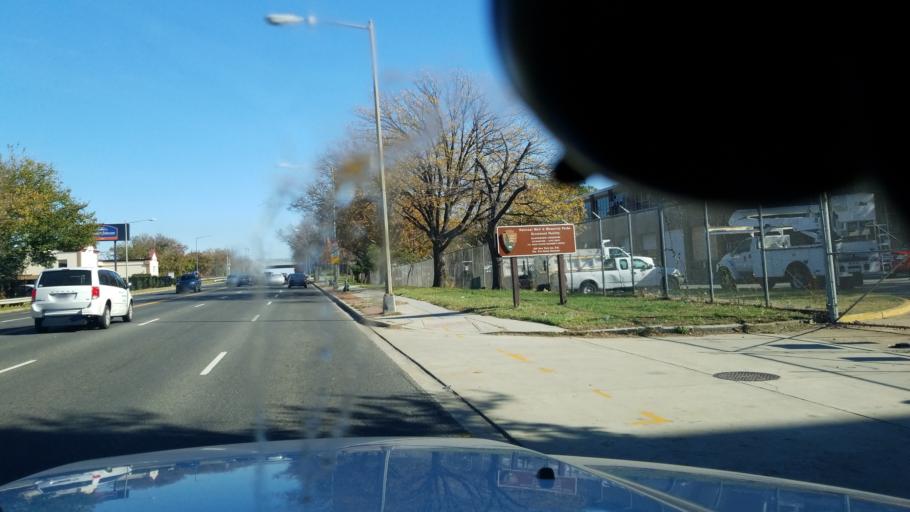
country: US
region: Washington, D.C.
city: Washington, D.C.
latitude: 38.9115
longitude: -76.9967
